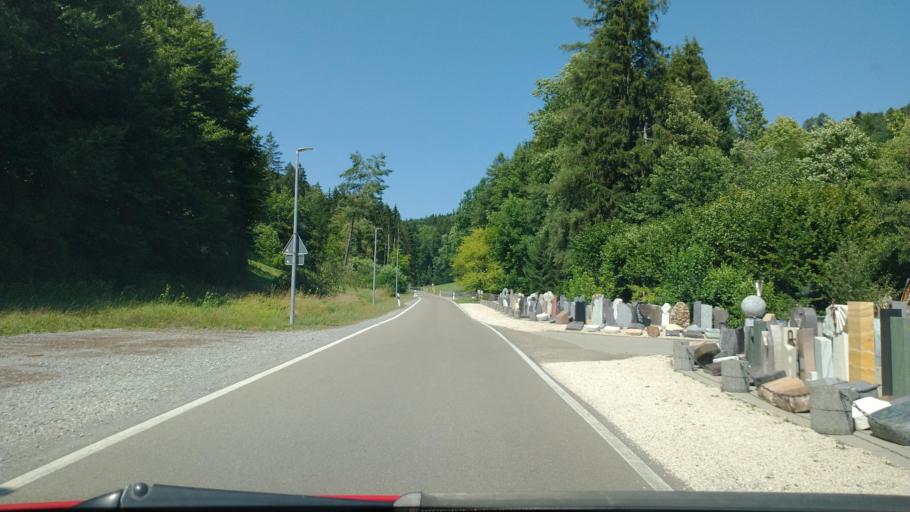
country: DE
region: Baden-Wuerttemberg
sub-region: Regierungsbezirk Stuttgart
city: Welzheim
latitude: 48.8386
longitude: 9.6353
